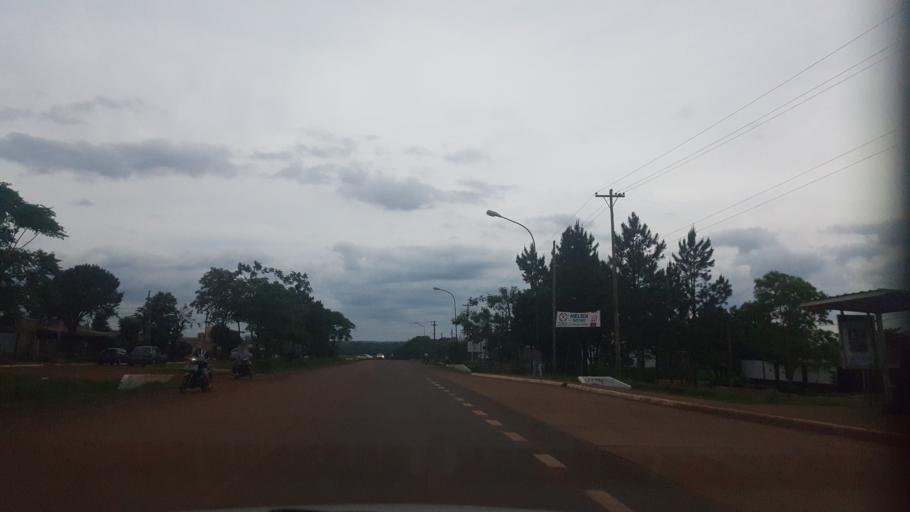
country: AR
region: Misiones
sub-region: Departamento de Candelaria
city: Candelaria
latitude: -27.4770
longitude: -55.7466
